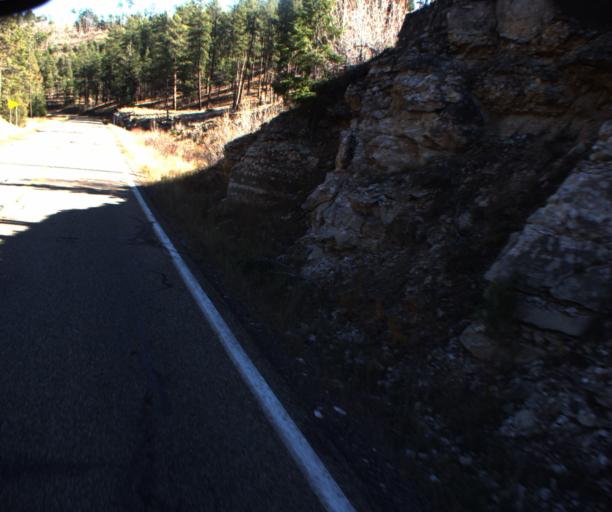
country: US
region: Arizona
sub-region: Coconino County
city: Fredonia
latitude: 36.7315
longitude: -112.1554
